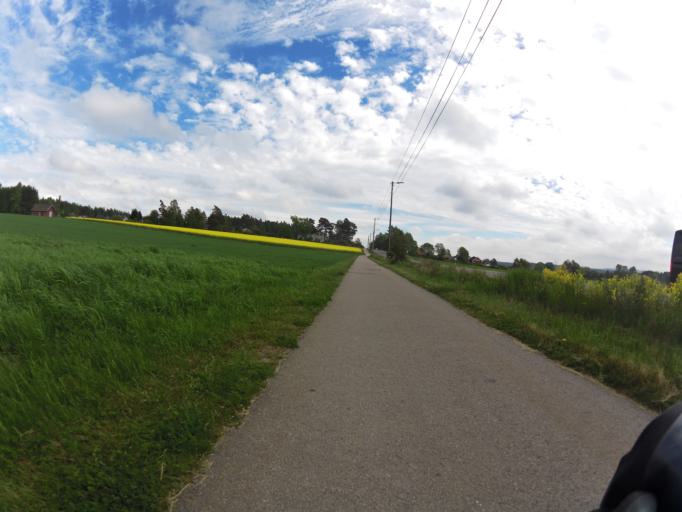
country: NO
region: Ostfold
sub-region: Rygge
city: Ryggebyen
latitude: 59.3665
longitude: 10.8067
